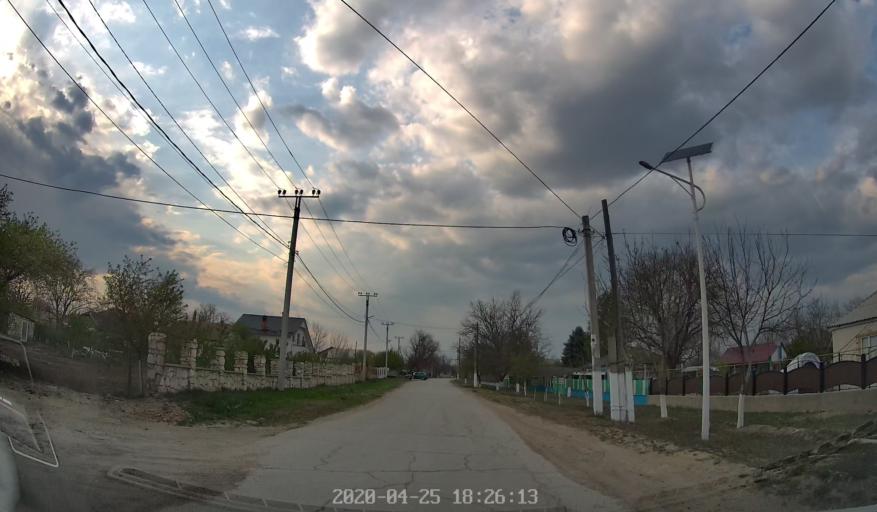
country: MD
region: Criuleni
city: Criuleni
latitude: 47.1657
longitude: 29.1271
